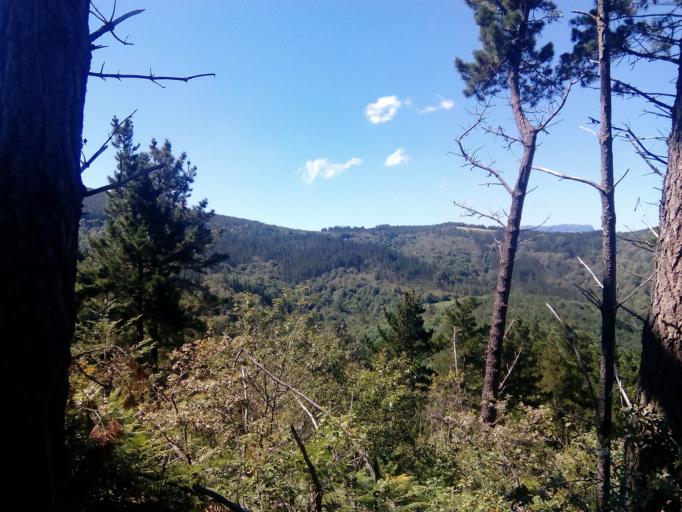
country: ES
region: Basque Country
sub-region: Provincia de Guipuzcoa
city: Lasarte
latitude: 43.2870
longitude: -2.0166
